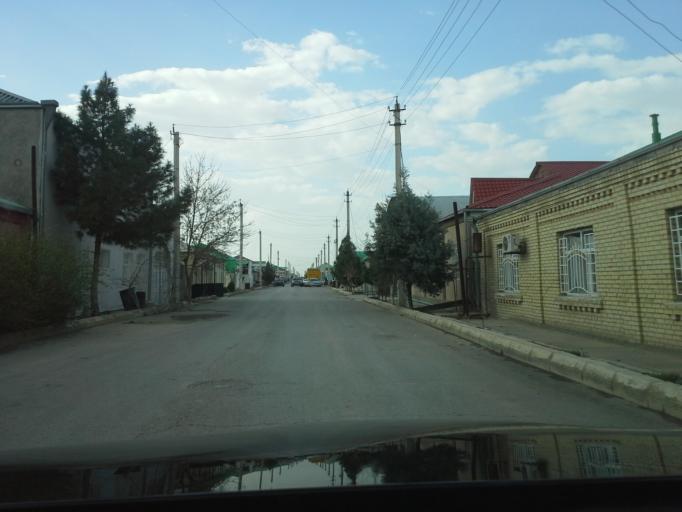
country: TM
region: Ahal
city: Ashgabat
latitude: 37.9894
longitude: 58.2957
